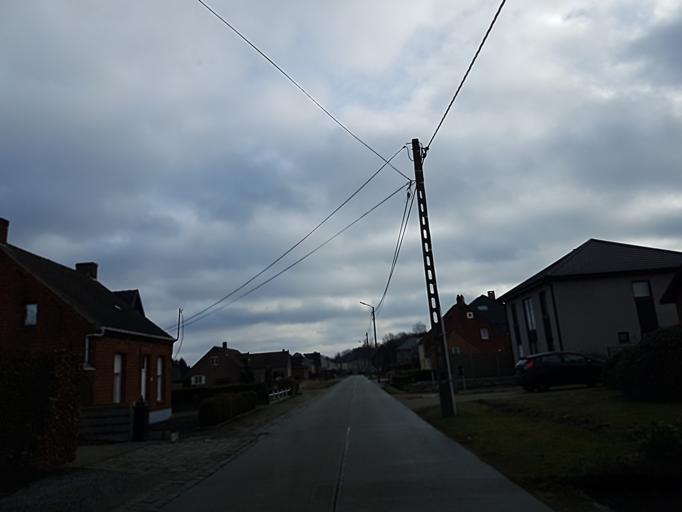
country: BE
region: Flanders
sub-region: Provincie Antwerpen
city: Hulshout
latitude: 51.0733
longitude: 4.8143
